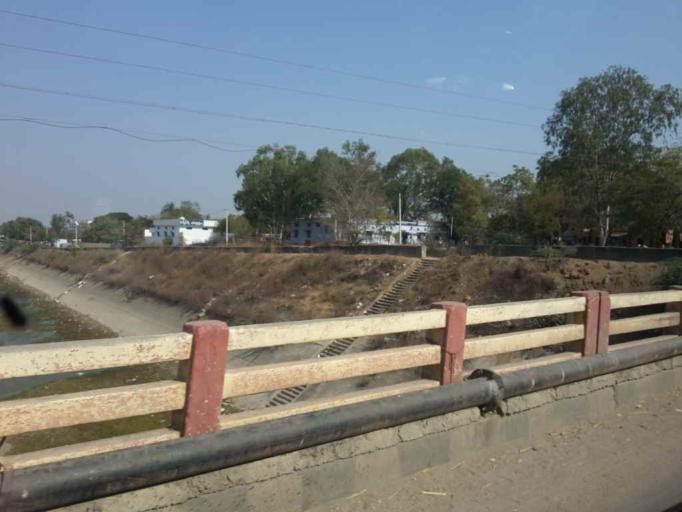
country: IN
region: Telangana
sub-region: Karimnagar
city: Koratla
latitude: 18.8487
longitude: 78.6177
